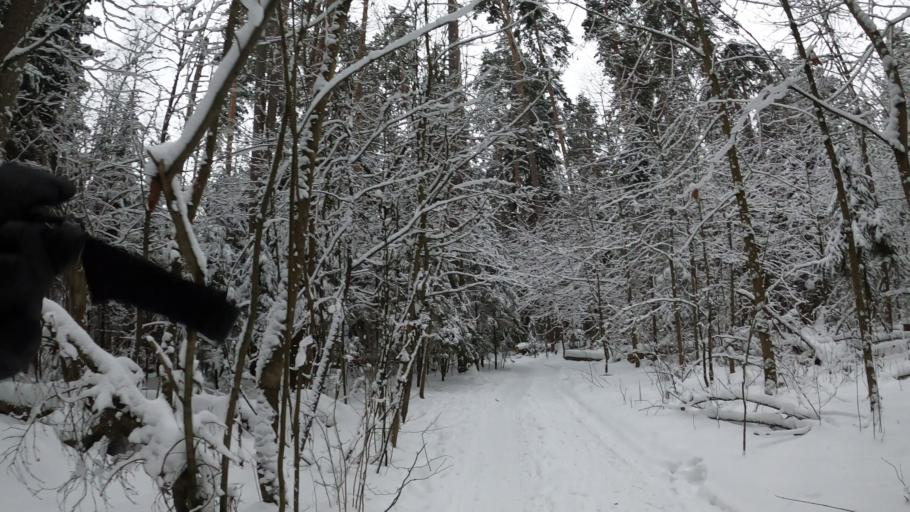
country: RU
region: Moskovskaya
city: Firsanovka
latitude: 55.9346
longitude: 37.2190
